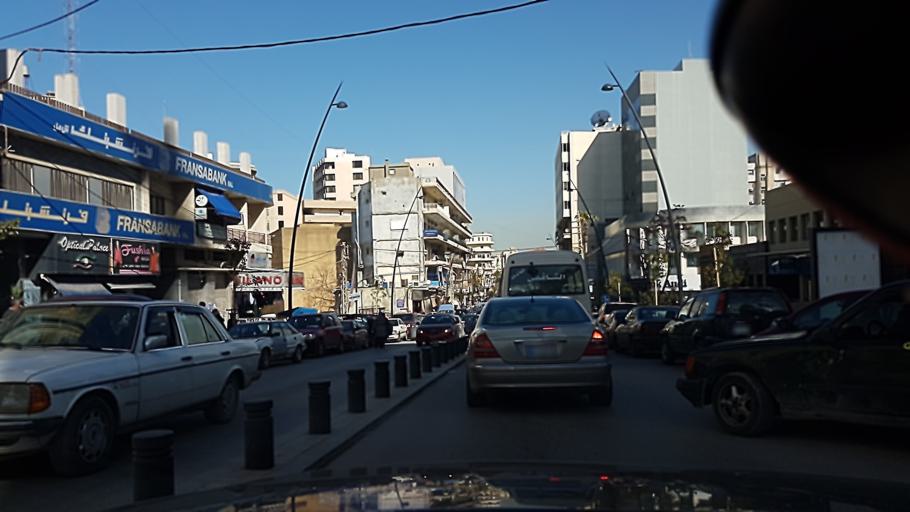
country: LB
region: Liban-Sud
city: Sidon
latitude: 33.5620
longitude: 35.3733
